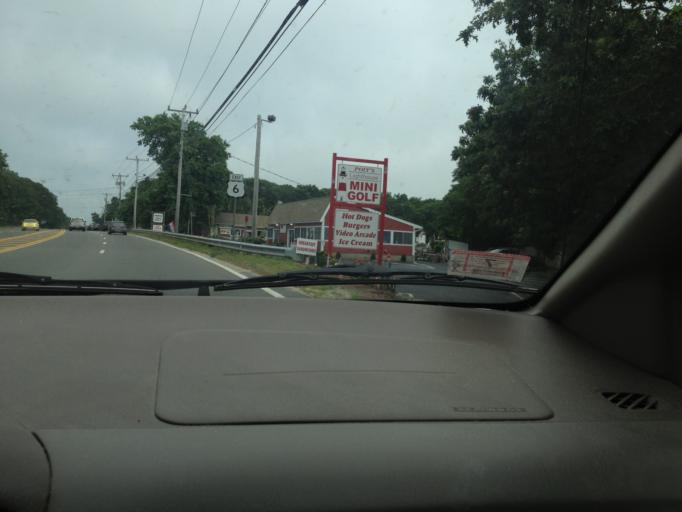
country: US
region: Massachusetts
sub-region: Barnstable County
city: North Eastham
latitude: 41.8668
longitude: -69.9845
